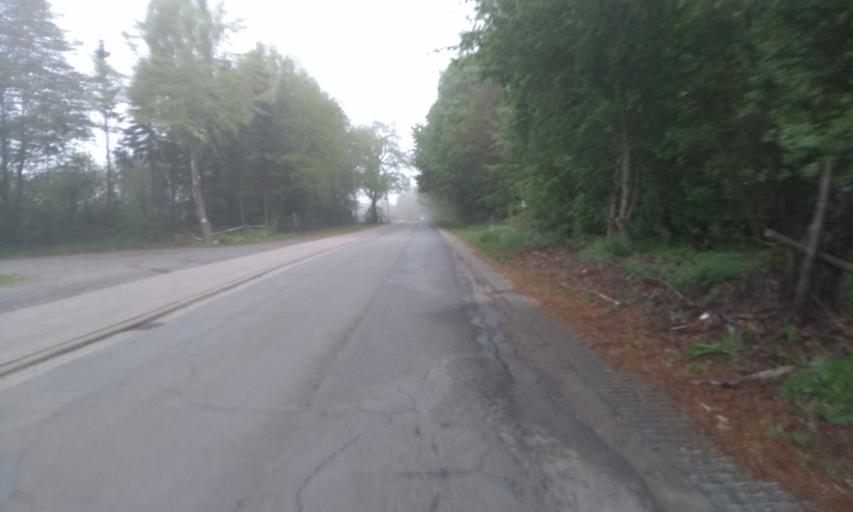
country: DE
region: Lower Saxony
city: Nottensdorf
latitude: 53.4718
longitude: 9.6162
